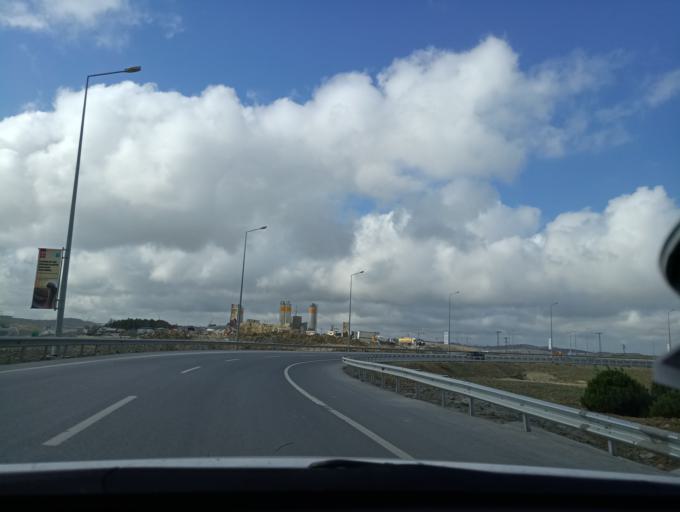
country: TR
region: Istanbul
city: Durusu
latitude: 41.2441
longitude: 28.7332
